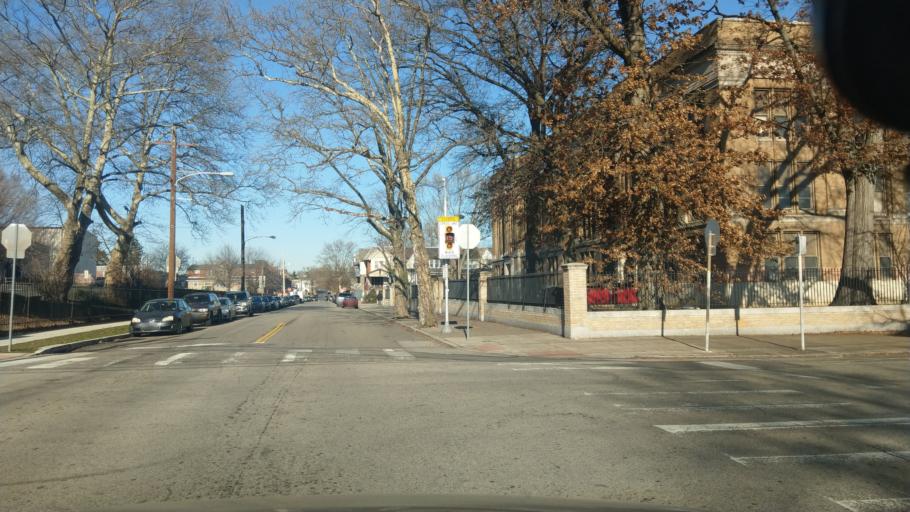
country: US
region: Pennsylvania
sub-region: Montgomery County
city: Wyncote
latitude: 40.0513
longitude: -75.1486
